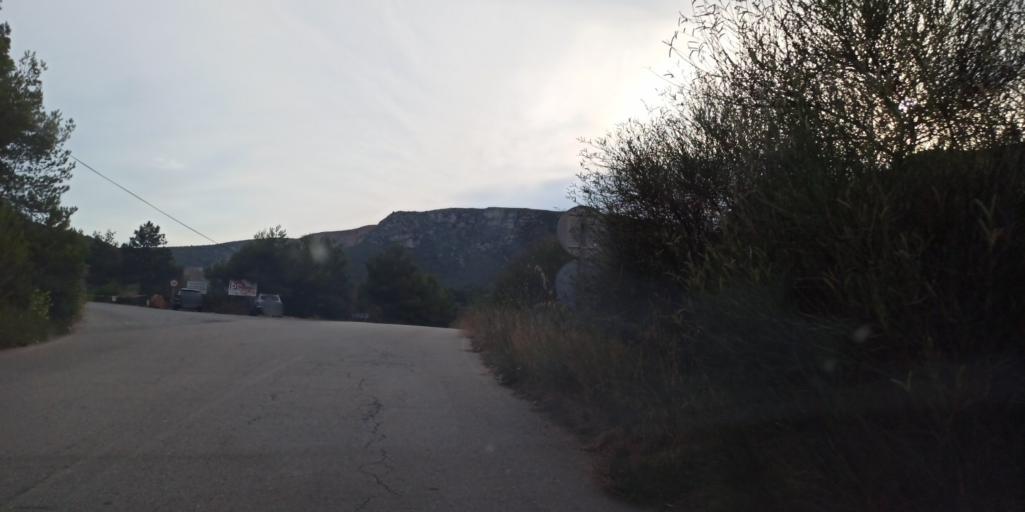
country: ES
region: Catalonia
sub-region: Provincia de Barcelona
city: Castelldefels
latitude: 41.2917
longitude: 1.9606
